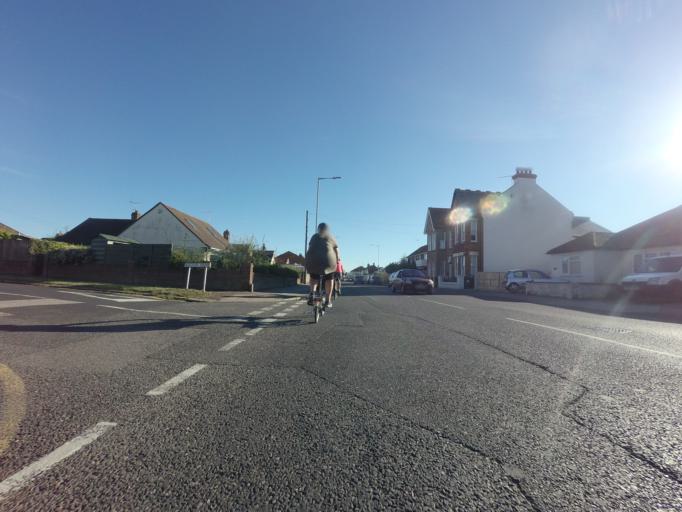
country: GB
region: England
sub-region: Kent
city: Herne Bay
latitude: 51.3676
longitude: 1.1124
